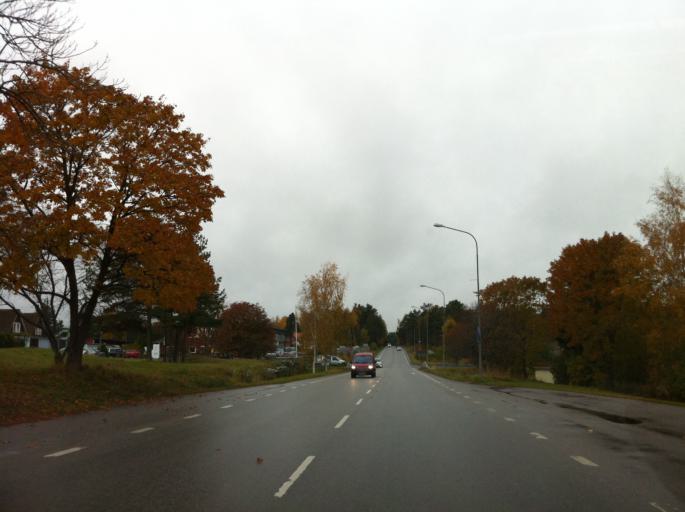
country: SE
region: Uppsala
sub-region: Osthammars Kommun
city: OEsthammar
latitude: 60.2598
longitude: 18.3590
